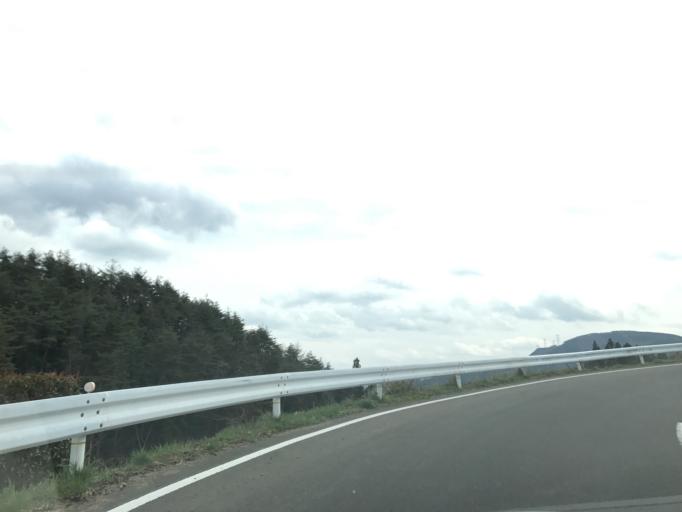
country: JP
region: Miyagi
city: Shiroishi
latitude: 38.0197
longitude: 140.5817
